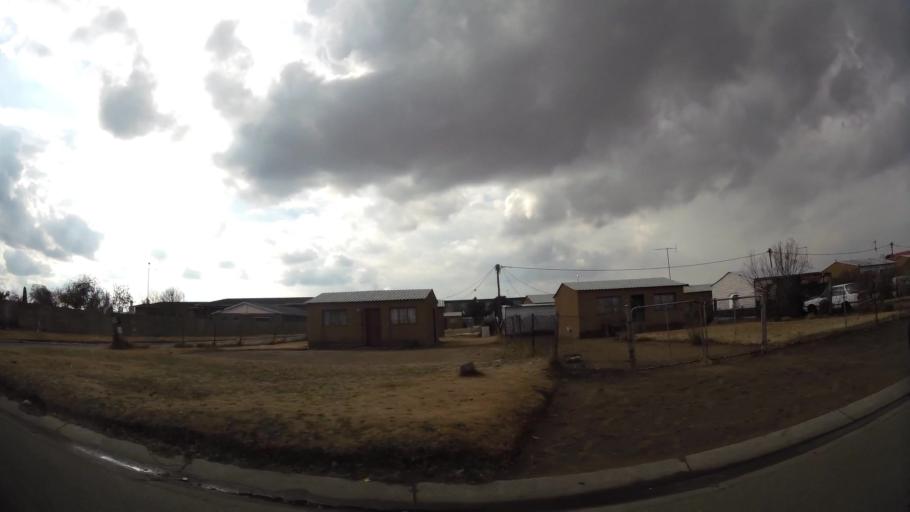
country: ZA
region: Orange Free State
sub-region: Fezile Dabi District Municipality
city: Sasolburg
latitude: -26.8396
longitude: 27.8525
